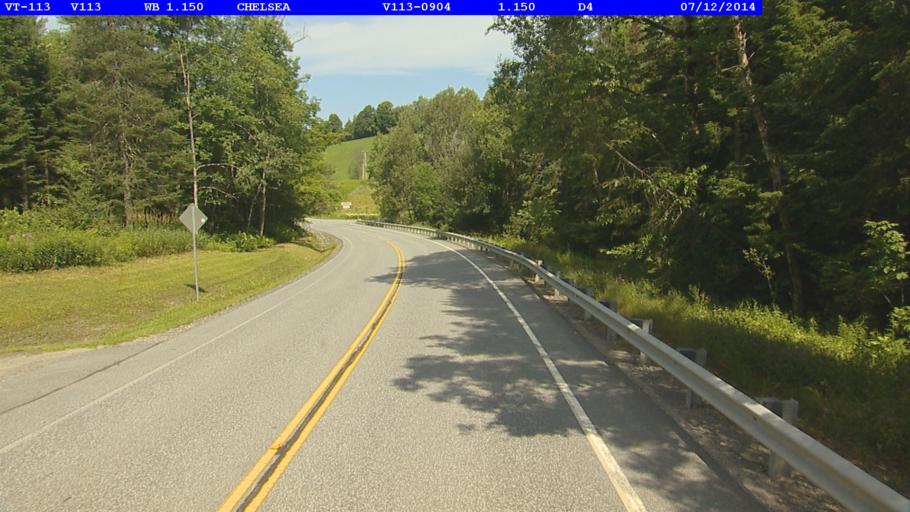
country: US
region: Vermont
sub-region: Orange County
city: Chelsea
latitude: 43.9925
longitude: -72.4281
